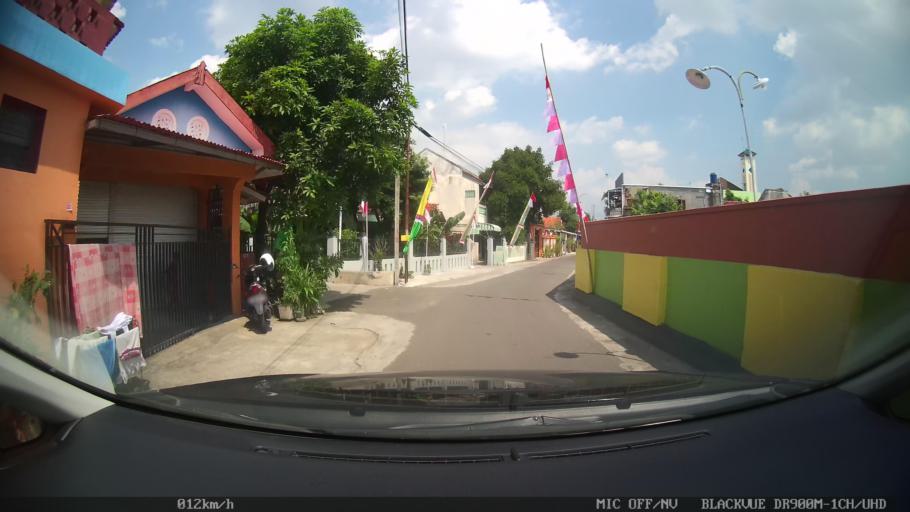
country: ID
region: Daerah Istimewa Yogyakarta
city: Depok
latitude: -7.8049
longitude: 110.4067
